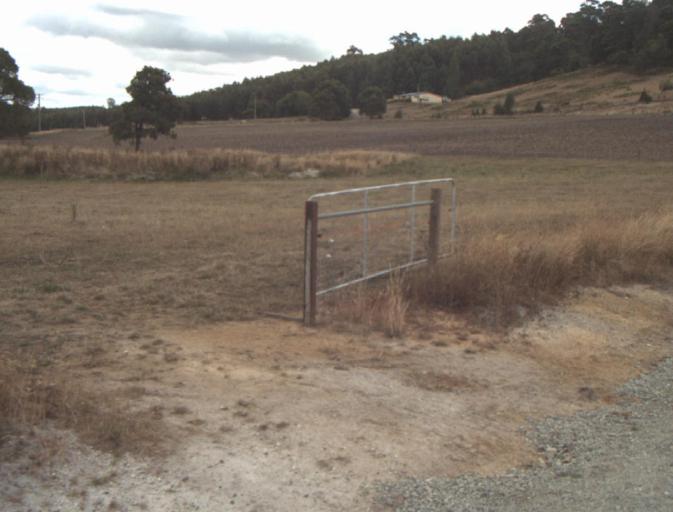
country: AU
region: Tasmania
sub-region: Launceston
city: Mayfield
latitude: -41.2013
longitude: 147.1895
